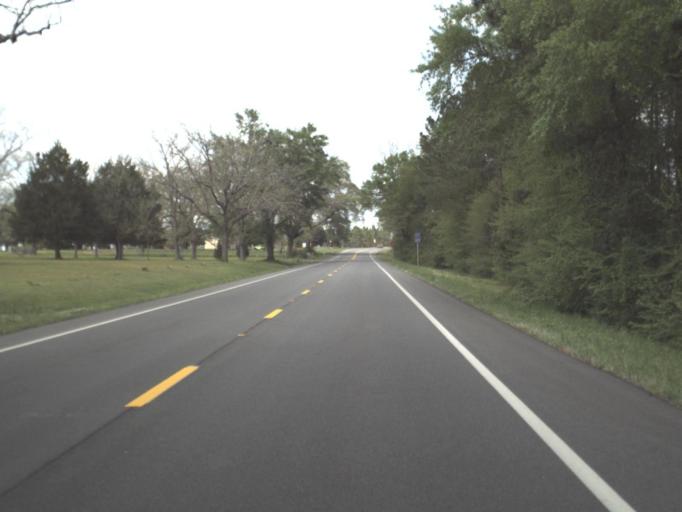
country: US
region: Alabama
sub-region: Covington County
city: Florala
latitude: 30.9466
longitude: -86.4776
